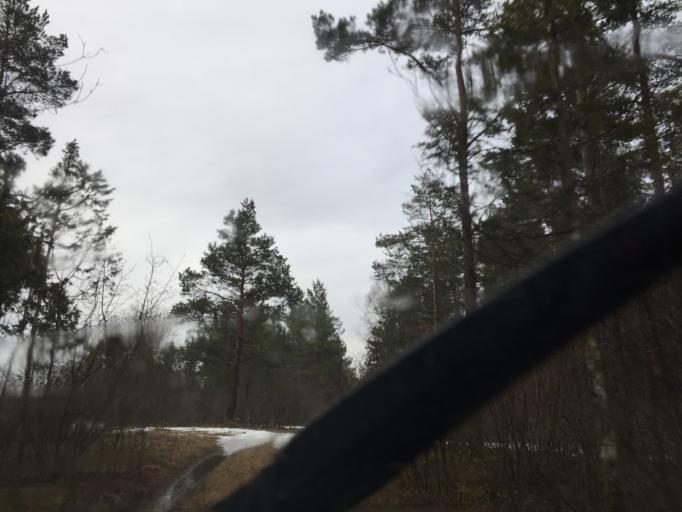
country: EE
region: Saare
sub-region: Orissaare vald
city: Orissaare
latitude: 58.6106
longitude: 22.9546
